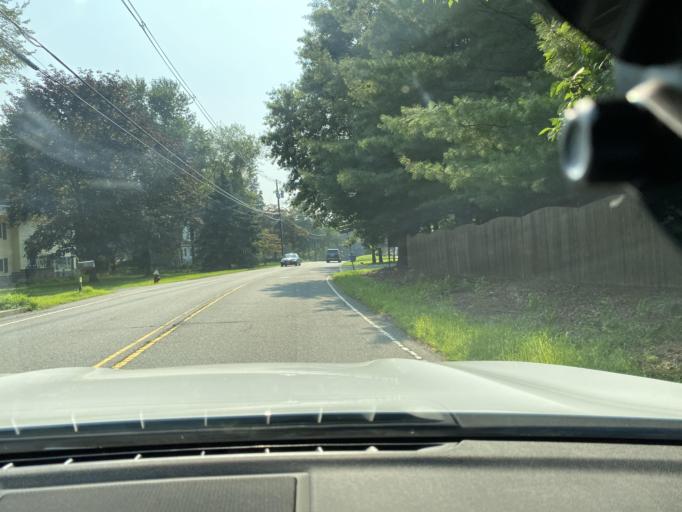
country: US
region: New York
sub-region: Rockland County
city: Airmont
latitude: 41.0814
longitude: -74.1198
